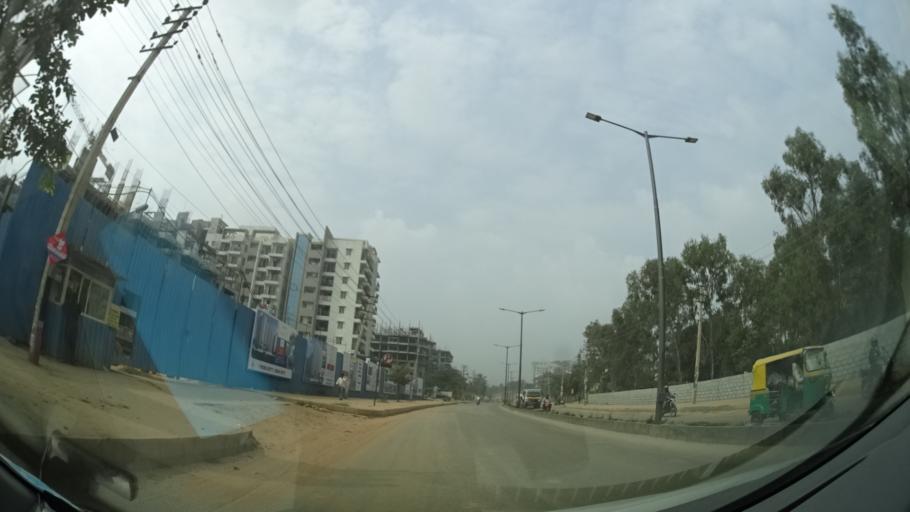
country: IN
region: Karnataka
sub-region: Bangalore Rural
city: Hoskote
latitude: 12.9827
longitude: 77.7564
